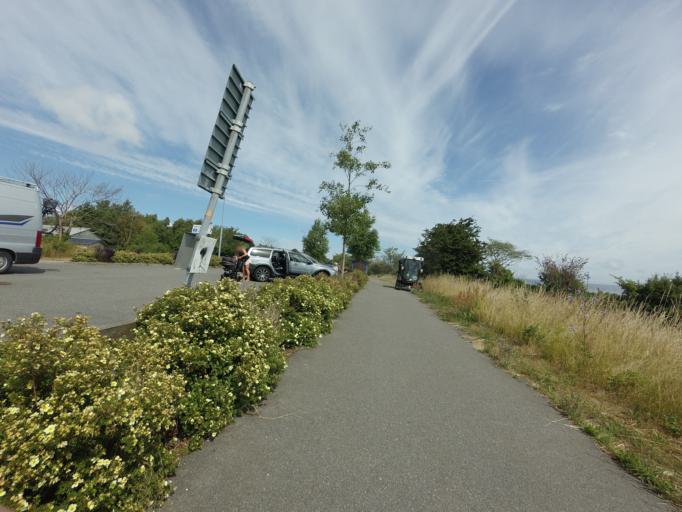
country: SE
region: Skane
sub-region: Simrishamns Kommun
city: Simrishamn
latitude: 55.5390
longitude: 14.3561
